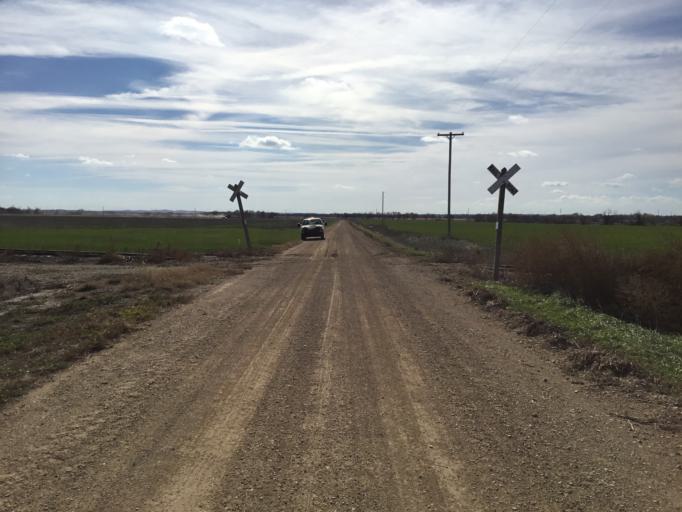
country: US
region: Kansas
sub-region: Lincoln County
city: Lincoln
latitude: 39.0513
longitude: -98.2213
